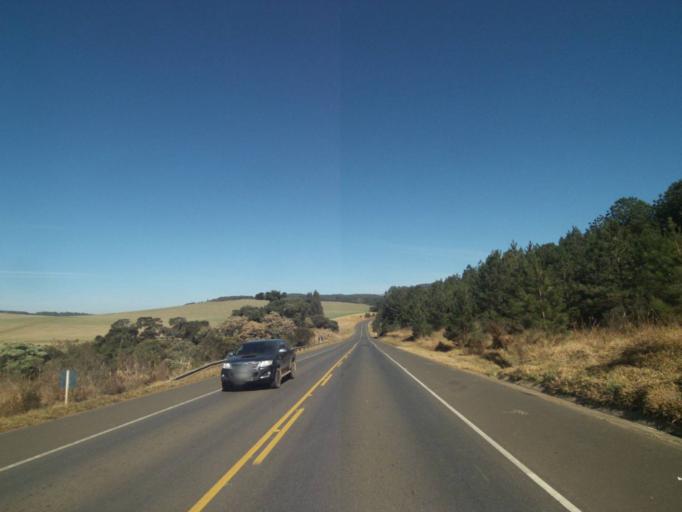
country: BR
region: Parana
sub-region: Tibagi
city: Tibagi
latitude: -24.5456
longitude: -50.4505
